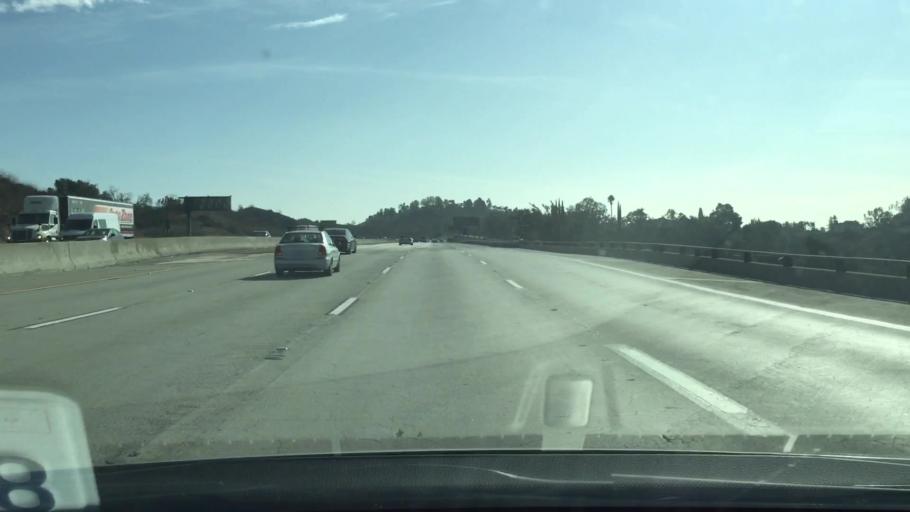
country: US
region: California
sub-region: Los Angeles County
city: San Dimas
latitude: 34.0927
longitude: -117.8197
